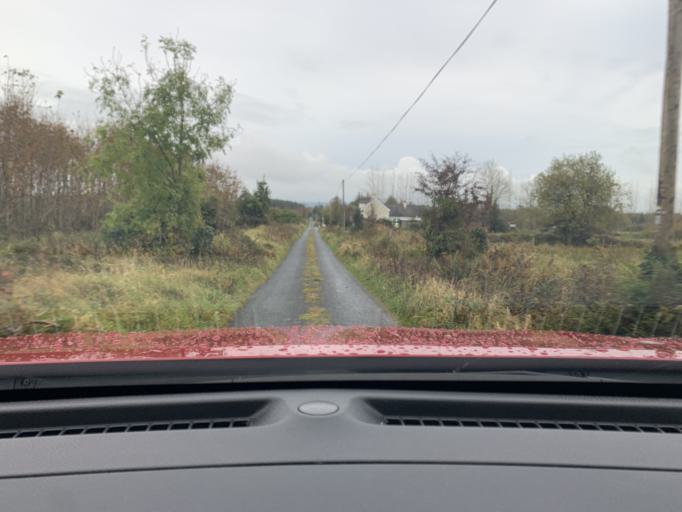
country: IE
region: Connaught
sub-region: Roscommon
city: Ballaghaderreen
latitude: 53.9232
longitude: -8.5621
